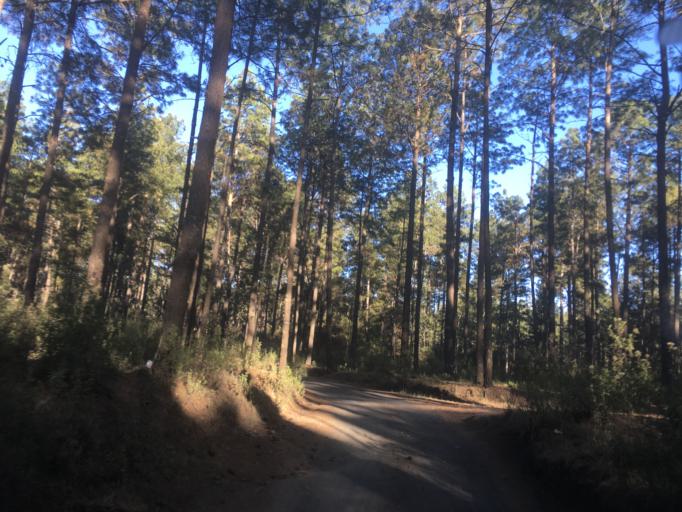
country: MX
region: Michoacan
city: Angahuan
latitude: 19.4628
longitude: -102.2245
